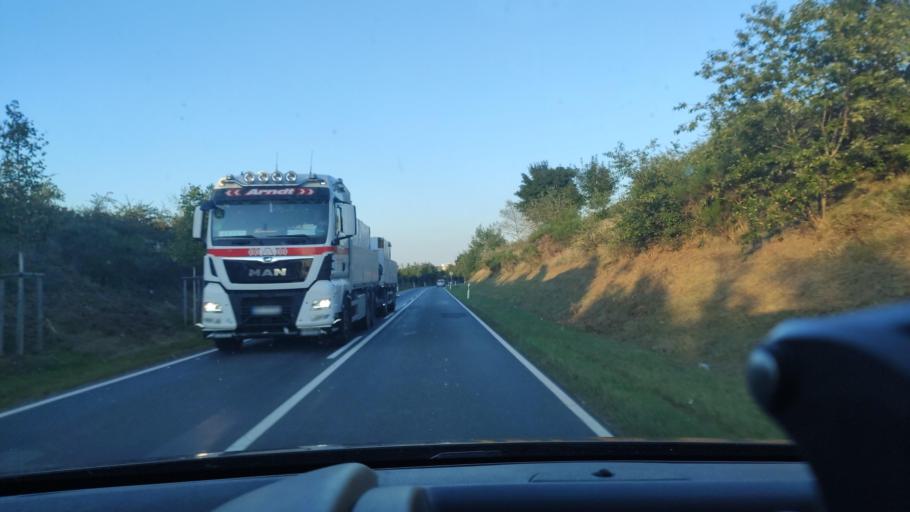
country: DE
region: Mecklenburg-Vorpommern
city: Lalendorf
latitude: 53.6194
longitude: 12.4165
